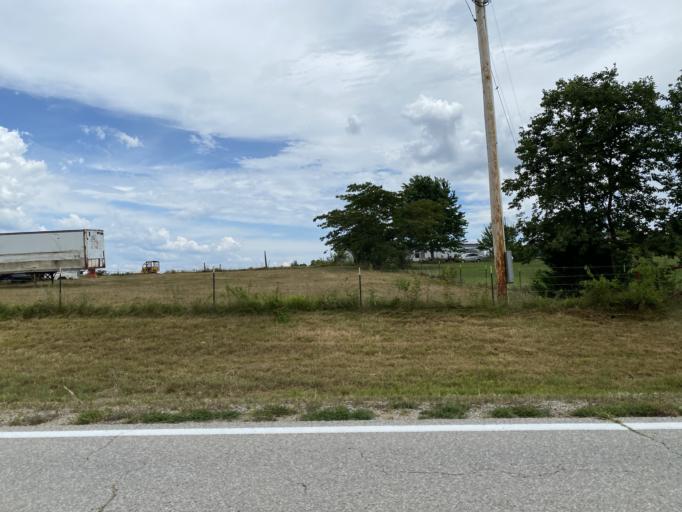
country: US
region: Arkansas
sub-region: Fulton County
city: Salem
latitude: 36.4309
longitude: -91.6979
